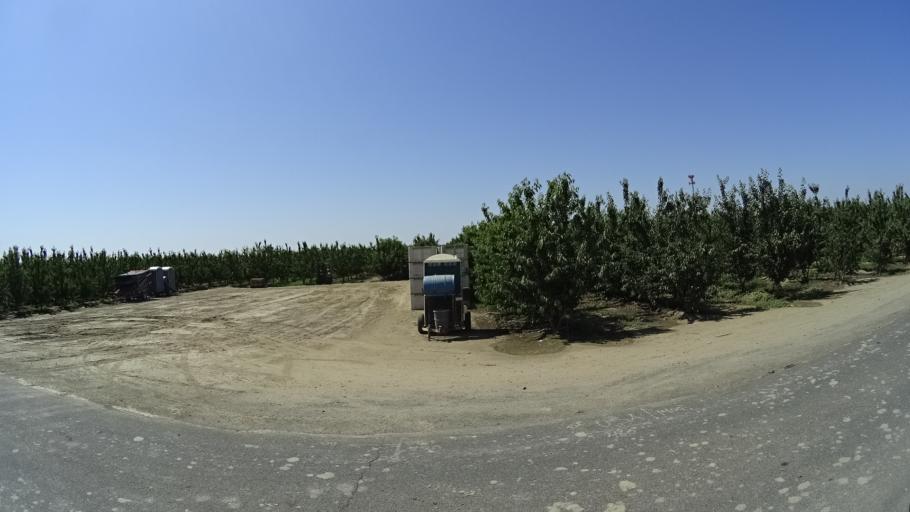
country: US
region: California
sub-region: Kings County
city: Lucerne
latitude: 36.3719
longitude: -119.6237
